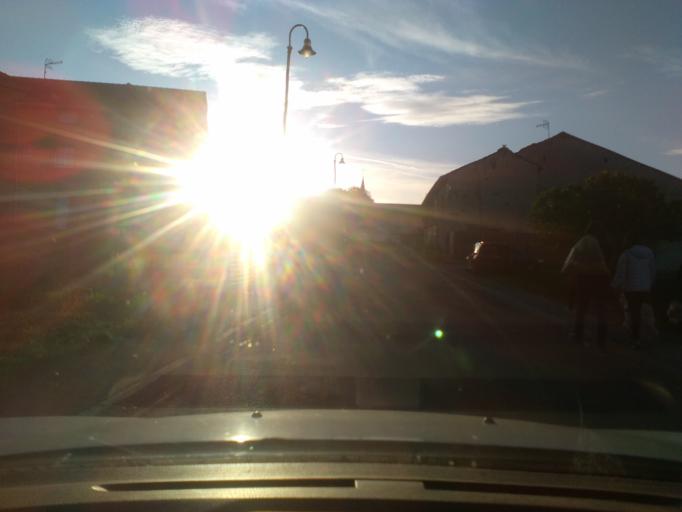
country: FR
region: Lorraine
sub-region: Departement des Vosges
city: Charmes
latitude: 48.3352
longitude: 6.2750
